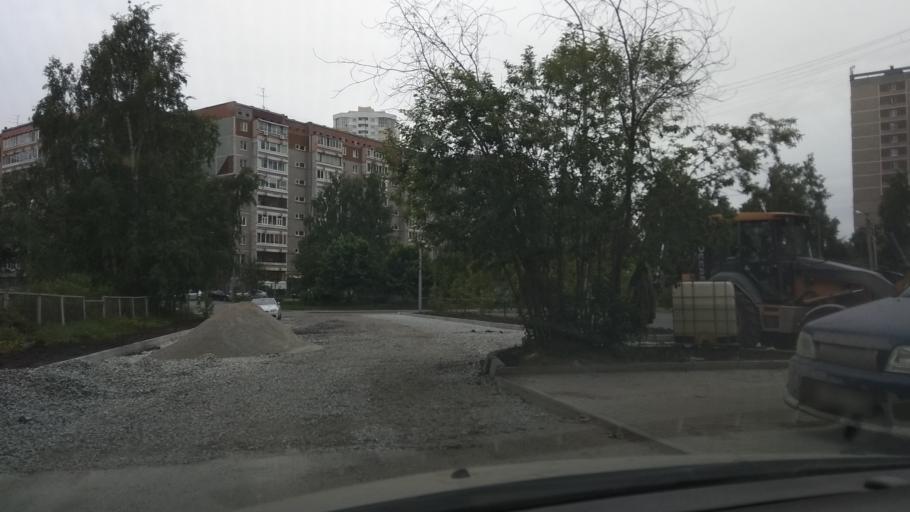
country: RU
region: Sverdlovsk
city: Sovkhoznyy
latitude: 56.7973
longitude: 60.5842
